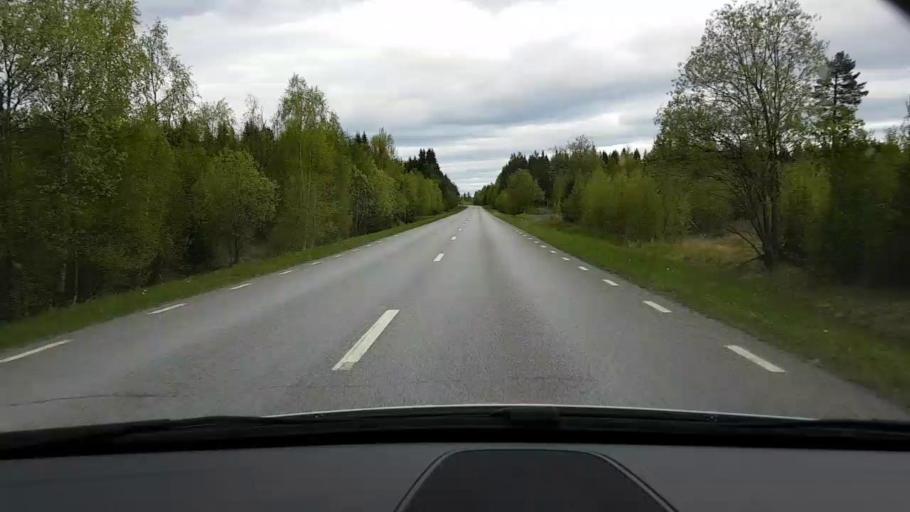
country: SE
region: Jaemtland
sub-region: Krokoms Kommun
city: Valla
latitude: 63.2313
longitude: 14.0121
